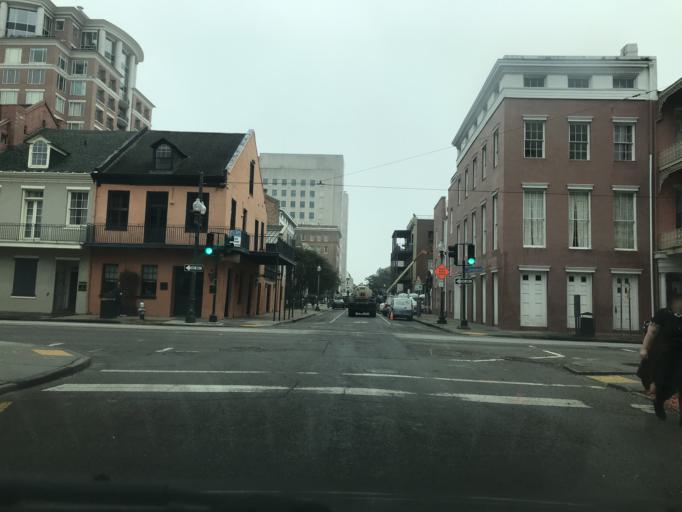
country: US
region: Louisiana
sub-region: Orleans Parish
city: New Orleans
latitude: 29.9477
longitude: -90.0727
